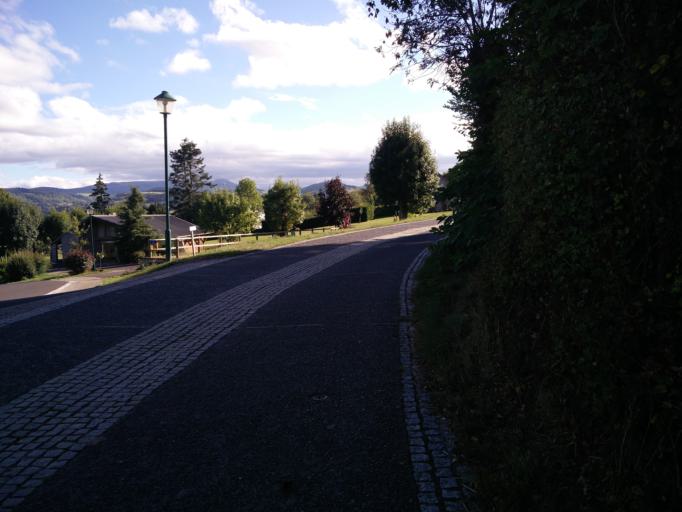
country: FR
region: Auvergne
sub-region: Departement du Puy-de-Dome
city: Gelles
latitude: 45.7255
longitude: 2.8251
